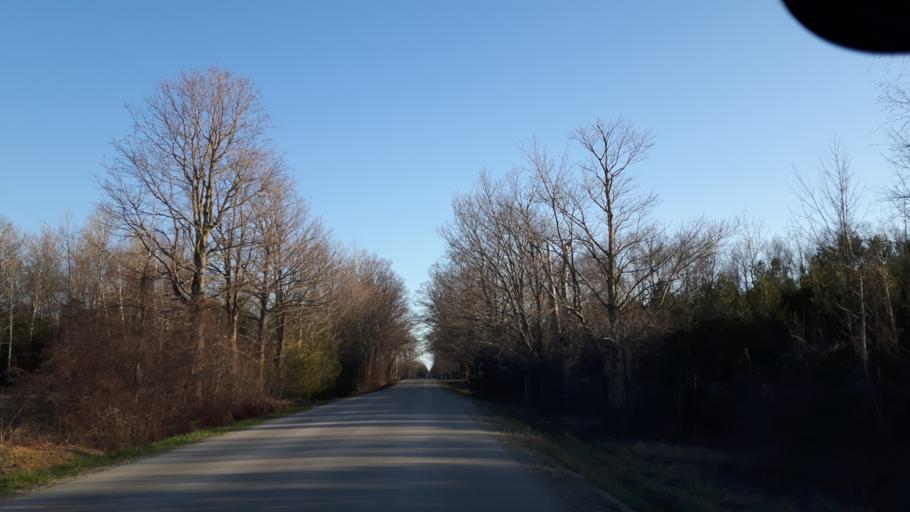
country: CA
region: Ontario
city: Goderich
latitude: 43.6268
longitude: -81.6847
